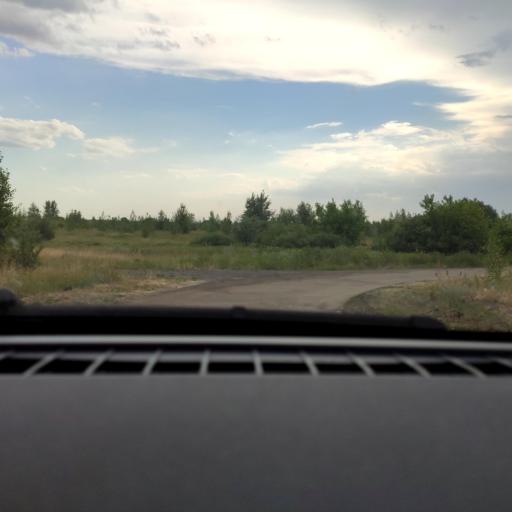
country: RU
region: Voronezj
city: Somovo
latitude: 51.7717
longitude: 39.3394
